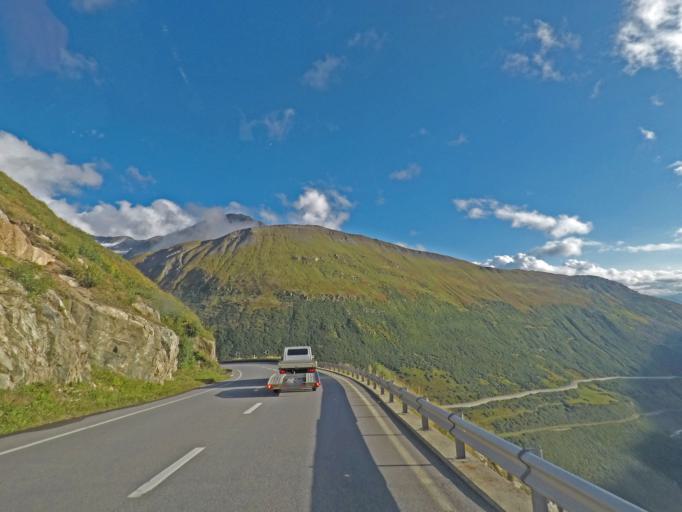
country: IT
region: Piedmont
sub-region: Provincia Verbano-Cusio-Ossola
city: Formazza
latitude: 46.5749
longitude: 8.3882
